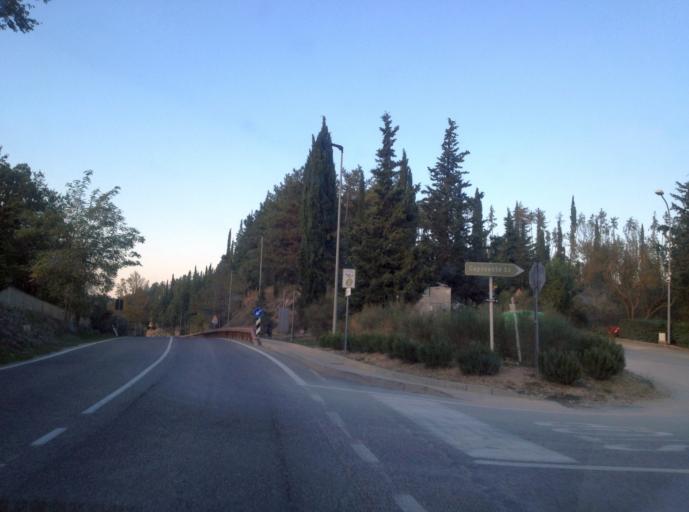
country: IT
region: Tuscany
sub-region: Provincia di Siena
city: Castellina in Chianti
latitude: 43.4566
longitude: 11.2924
